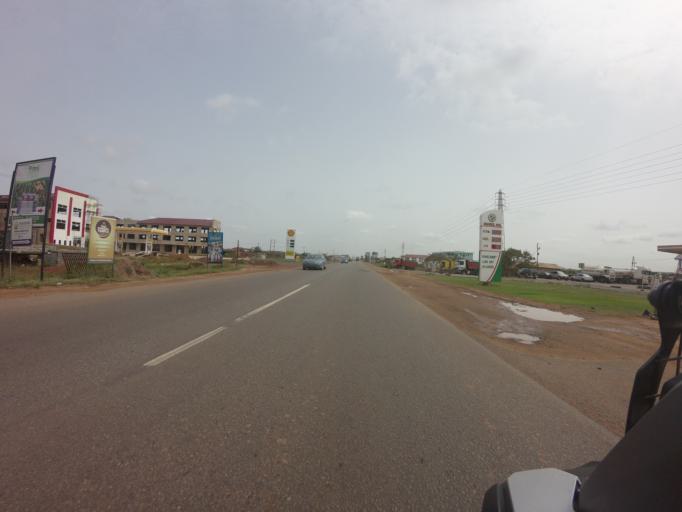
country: GH
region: Greater Accra
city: Tema
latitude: 5.7432
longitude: 0.0371
